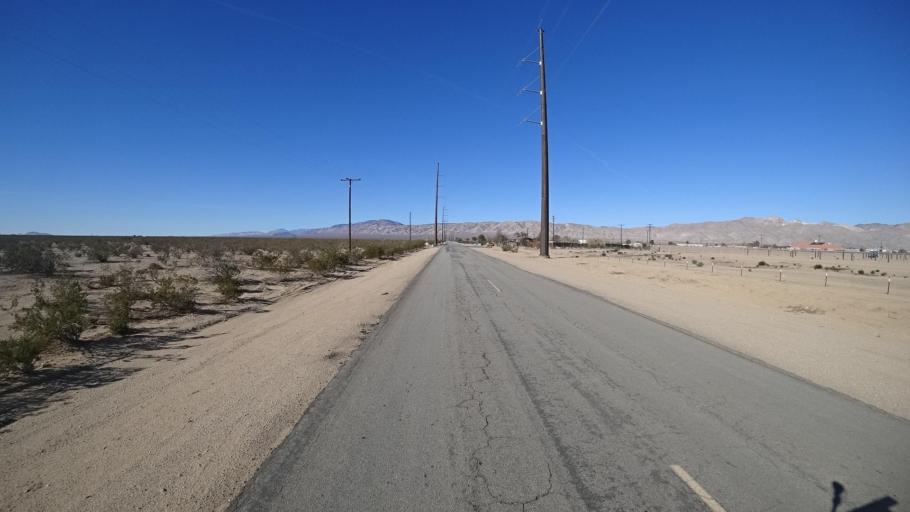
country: US
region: California
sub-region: Kern County
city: California City
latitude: 35.1987
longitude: -118.0112
